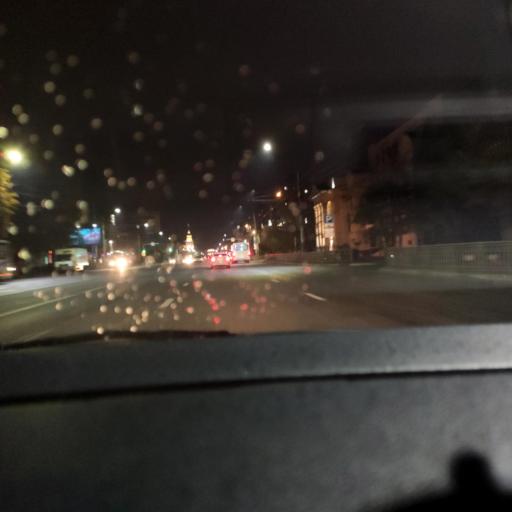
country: RU
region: Voronezj
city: Voronezh
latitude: 51.6510
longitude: 39.1929
